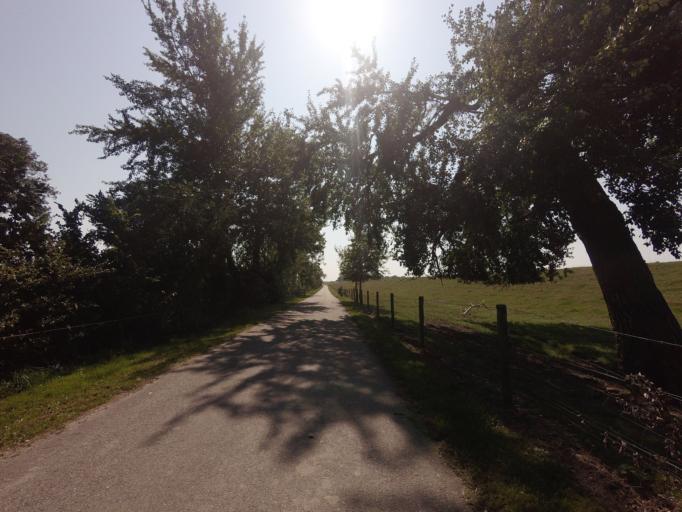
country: NL
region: Groningen
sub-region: Gemeente De Marne
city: Ulrum
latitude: 53.3484
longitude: 6.2968
